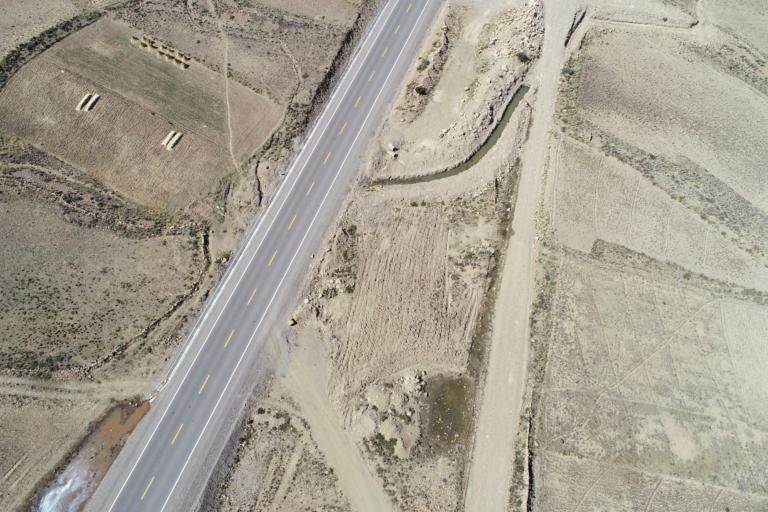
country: BO
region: La Paz
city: Achacachi
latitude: -15.8877
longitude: -68.8100
